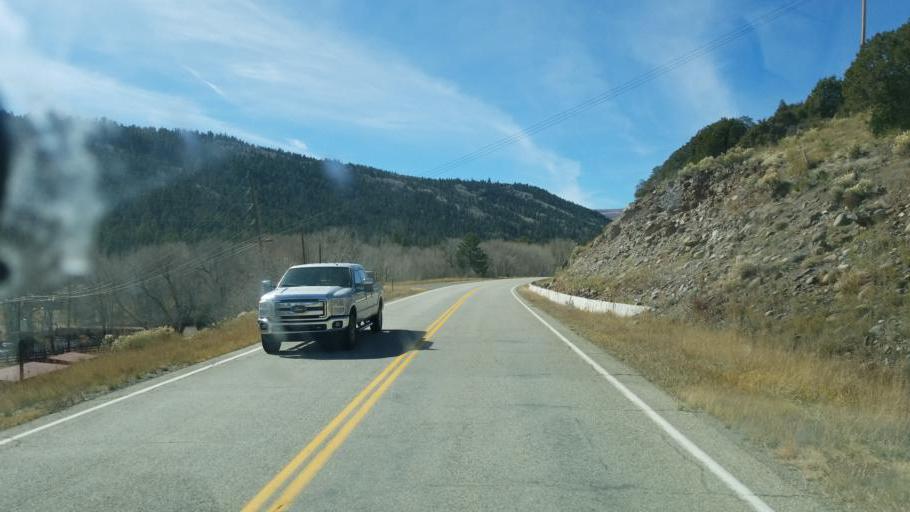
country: US
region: Colorado
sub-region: Conejos County
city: Conejos
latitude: 37.0686
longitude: -106.2470
